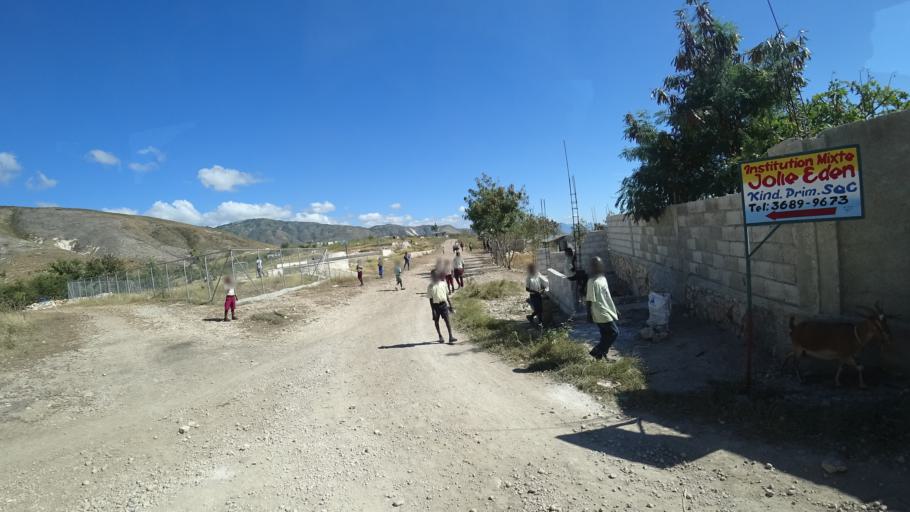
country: HT
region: Ouest
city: Croix des Bouquets
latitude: 18.6719
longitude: -72.2737
